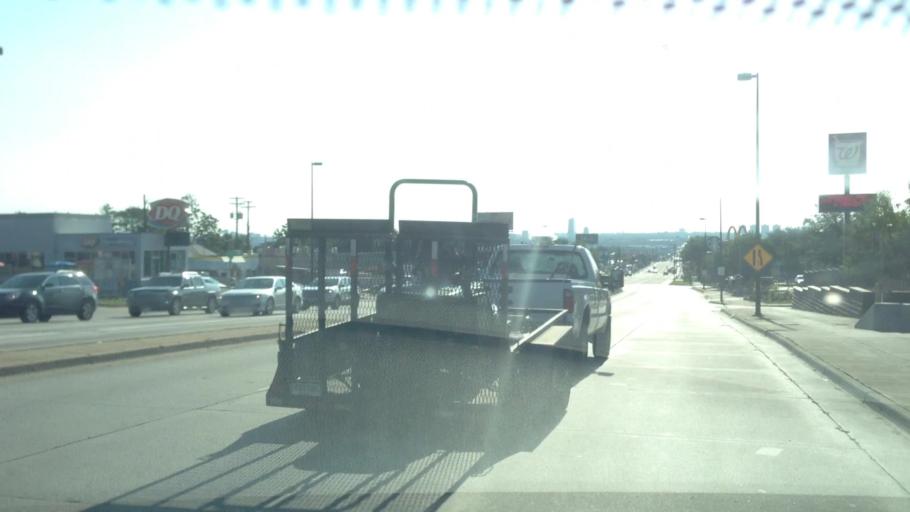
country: US
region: Colorado
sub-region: Denver County
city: Denver
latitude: 39.7110
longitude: -105.0249
